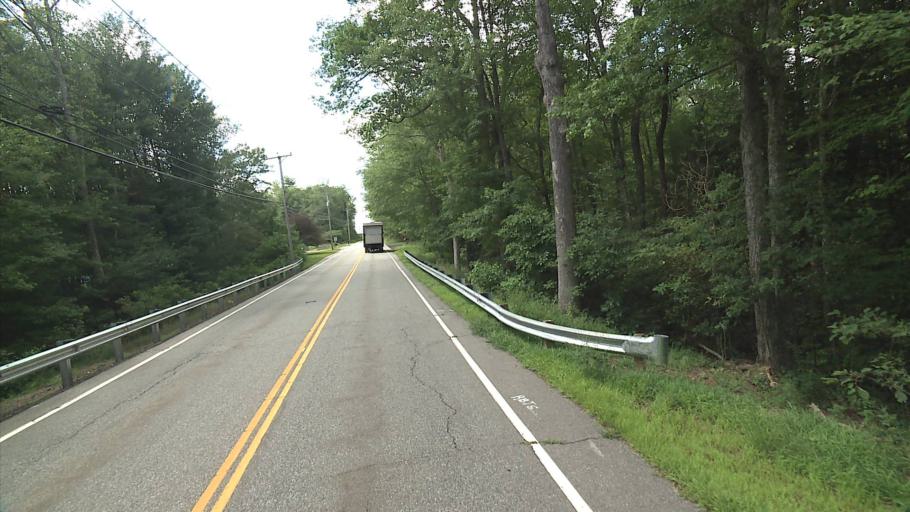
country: US
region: Connecticut
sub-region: Tolland County
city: Stafford
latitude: 41.9622
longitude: -72.2338
